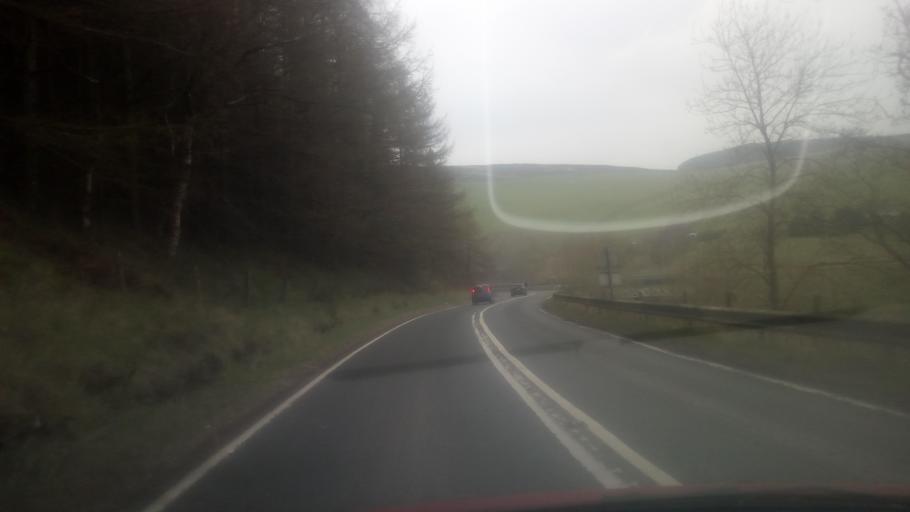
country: GB
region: Scotland
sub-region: The Scottish Borders
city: Galashiels
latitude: 55.7050
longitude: -2.8879
